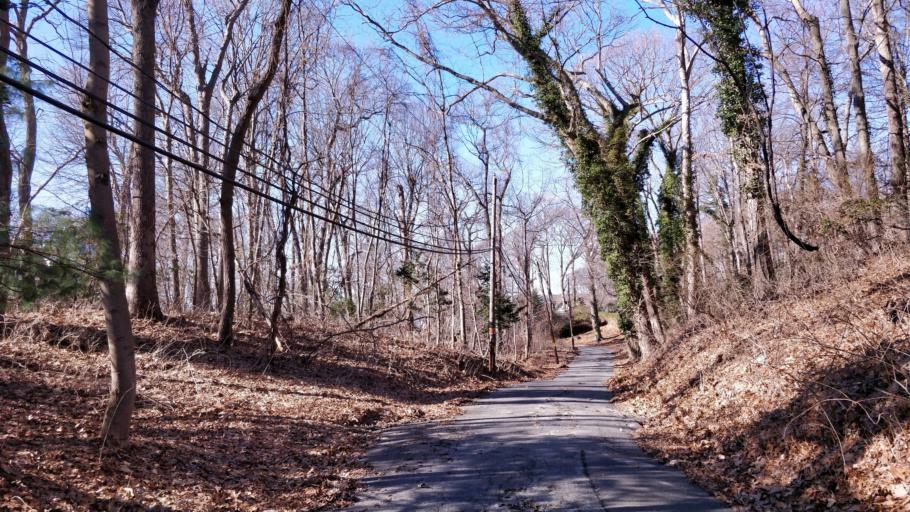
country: US
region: New York
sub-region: Suffolk County
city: Port Jefferson
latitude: 40.9604
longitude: -73.0717
